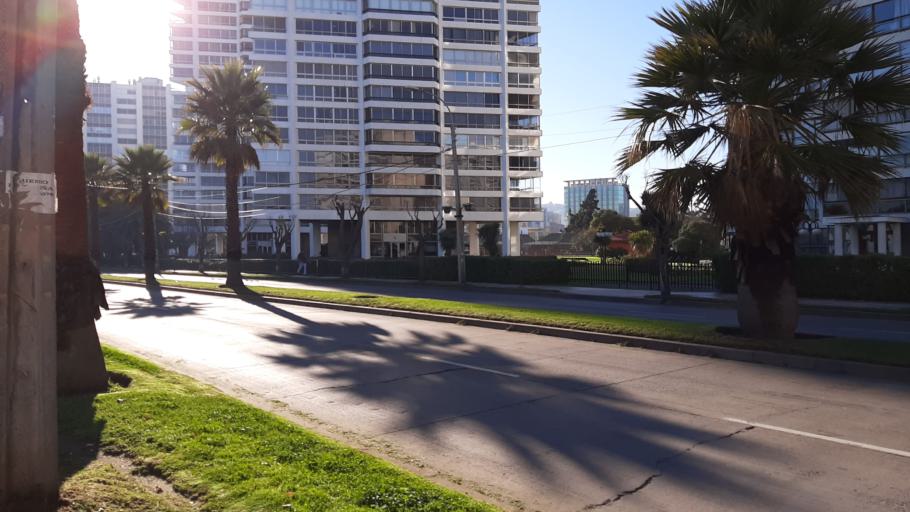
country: CL
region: Valparaiso
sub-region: Provincia de Valparaiso
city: Vina del Mar
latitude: -33.0120
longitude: -71.5532
